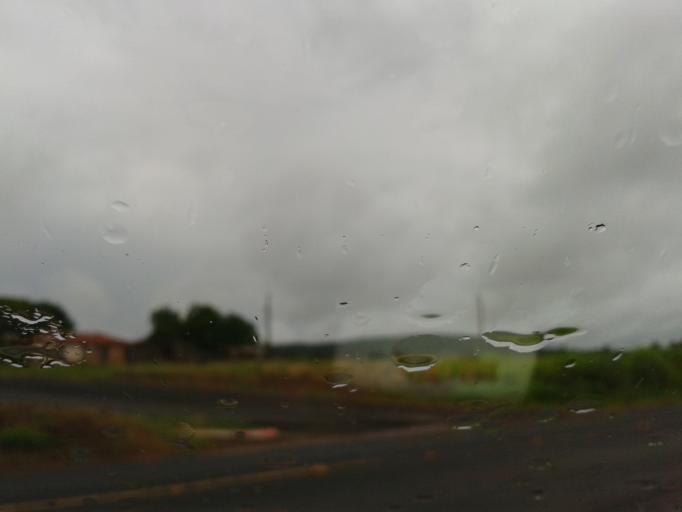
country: BR
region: Minas Gerais
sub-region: Santa Vitoria
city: Santa Vitoria
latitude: -19.2722
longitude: -50.0046
